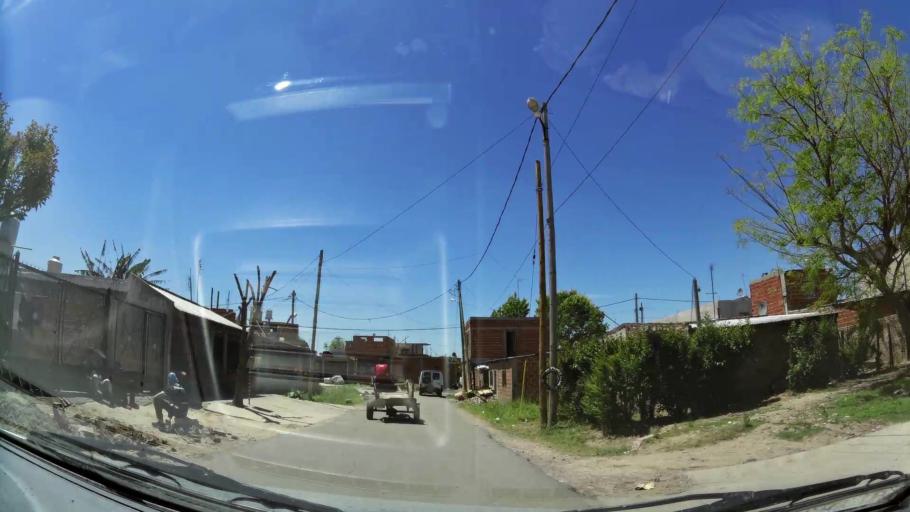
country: AR
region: Buenos Aires
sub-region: Partido de Lanus
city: Lanus
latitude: -34.7235
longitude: -58.3258
